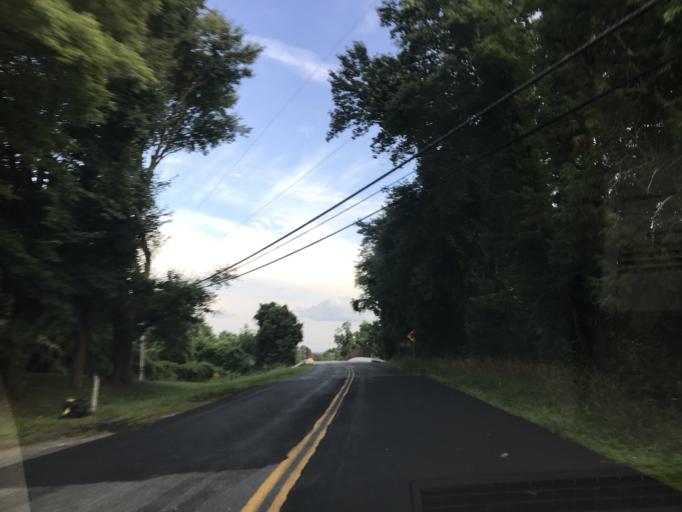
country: US
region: Maryland
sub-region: Harford County
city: Aberdeen
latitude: 39.5145
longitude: -76.2071
